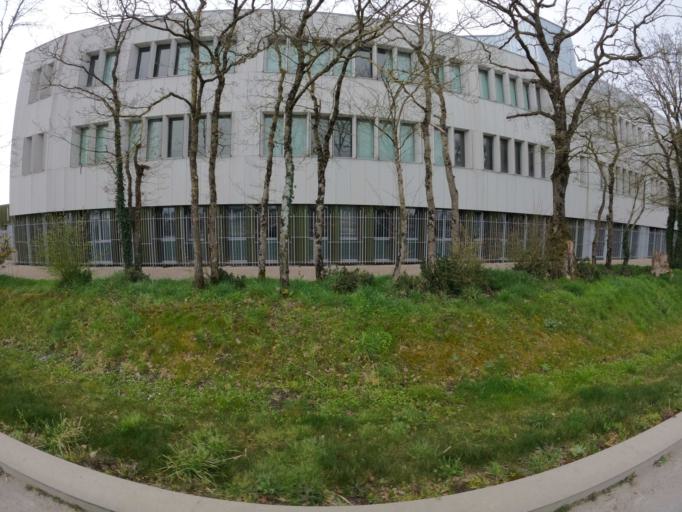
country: FR
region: Pays de la Loire
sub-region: Departement de la Vendee
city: Montaigu
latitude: 46.9847
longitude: -1.3090
